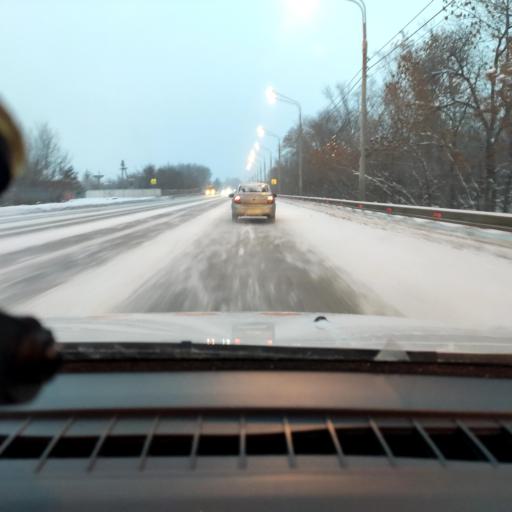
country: RU
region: Samara
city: Otradnyy
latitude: 53.3657
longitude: 51.3566
